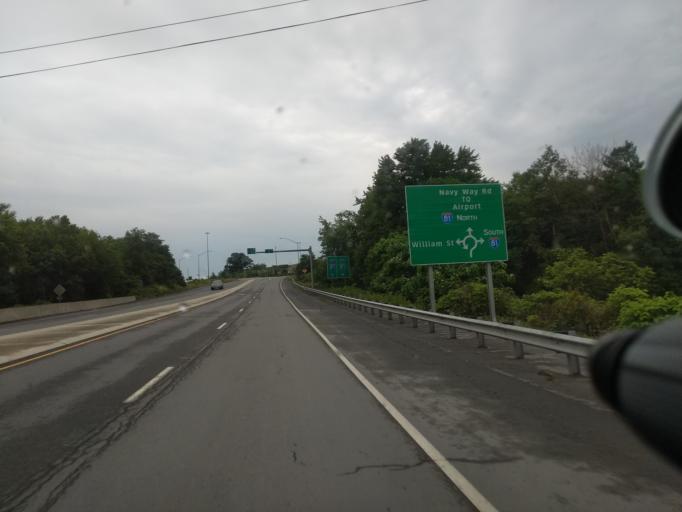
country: US
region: Pennsylvania
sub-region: Luzerne County
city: Dupont
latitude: 41.3324
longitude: -75.7408
